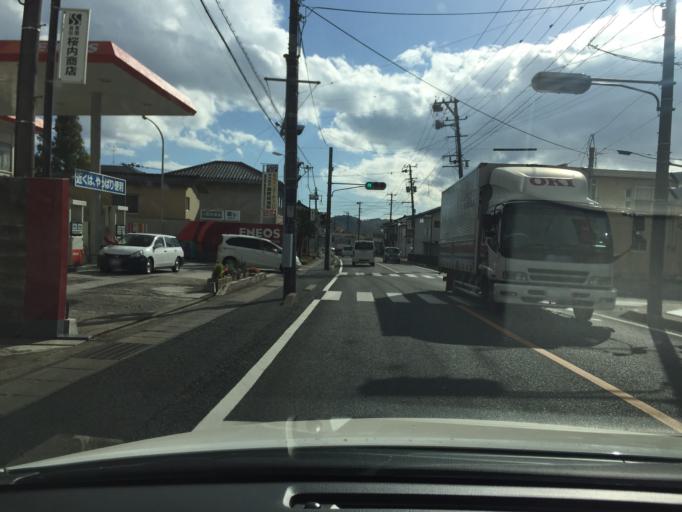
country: JP
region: Fukushima
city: Nihommatsu
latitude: 37.6578
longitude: 140.4607
